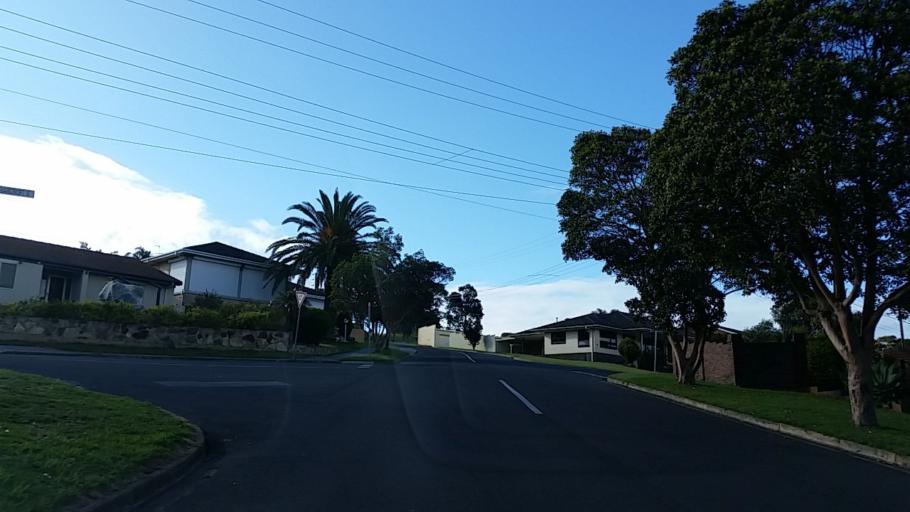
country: AU
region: South Australia
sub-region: Marion
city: Clovelly Park
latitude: -35.0077
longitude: 138.5880
